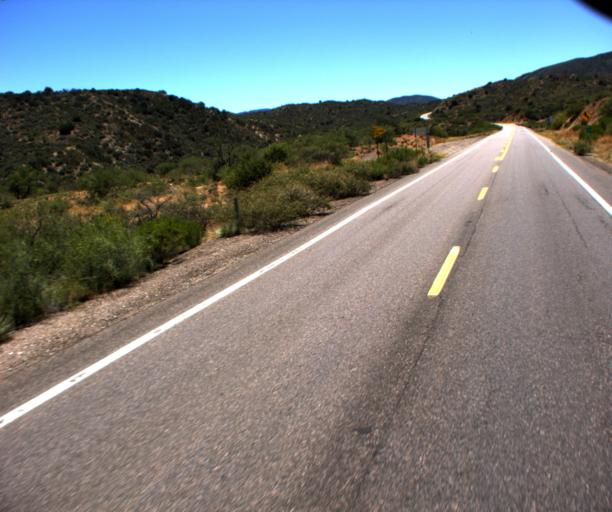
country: US
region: Arizona
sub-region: Gila County
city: Globe
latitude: 33.3200
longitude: -110.7351
